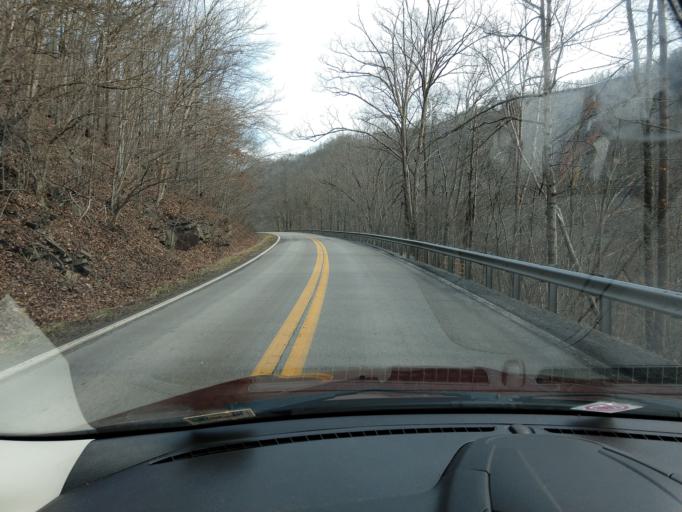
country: US
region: West Virginia
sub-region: McDowell County
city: Welch
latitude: 37.3181
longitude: -81.7169
